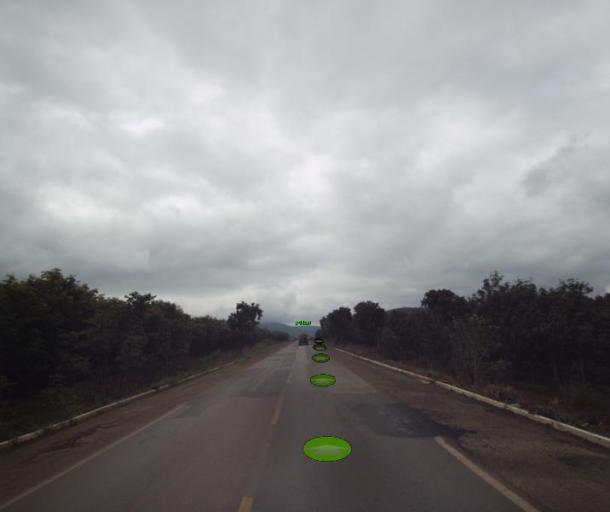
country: BR
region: Goias
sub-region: Barro Alto
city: Barro Alto
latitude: -14.8763
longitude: -48.9965
